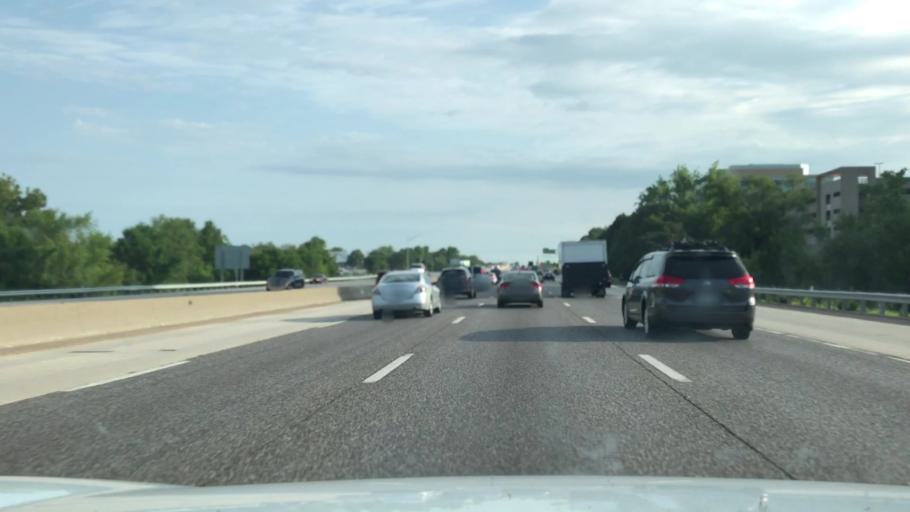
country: US
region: Missouri
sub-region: Saint Louis County
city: Maryland Heights
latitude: 38.7091
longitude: -90.4486
